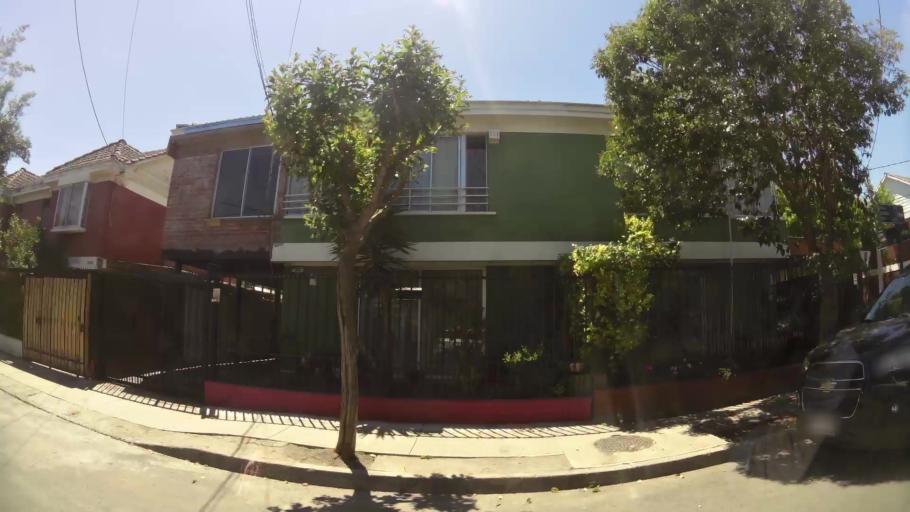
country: CL
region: Santiago Metropolitan
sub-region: Provincia de Maipo
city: San Bernardo
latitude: -33.6210
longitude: -70.7122
